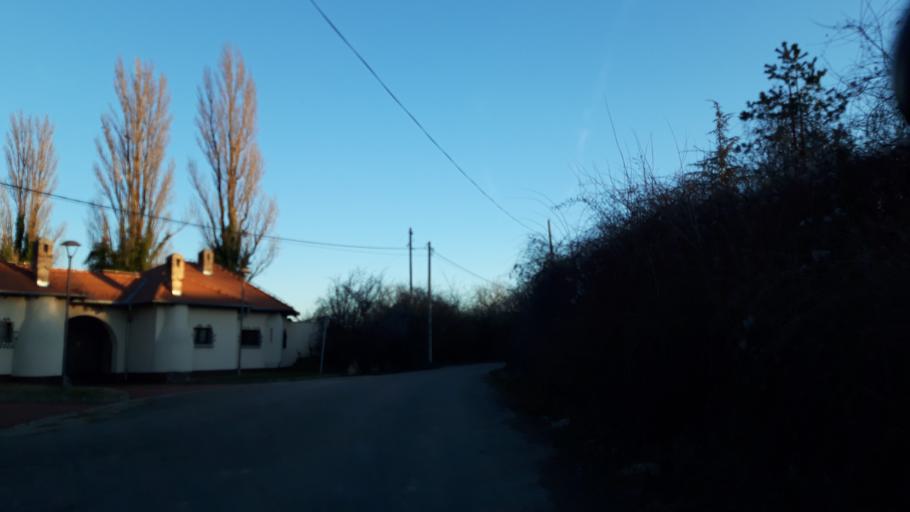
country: RS
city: Cortanovci
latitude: 45.1649
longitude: 19.9994
